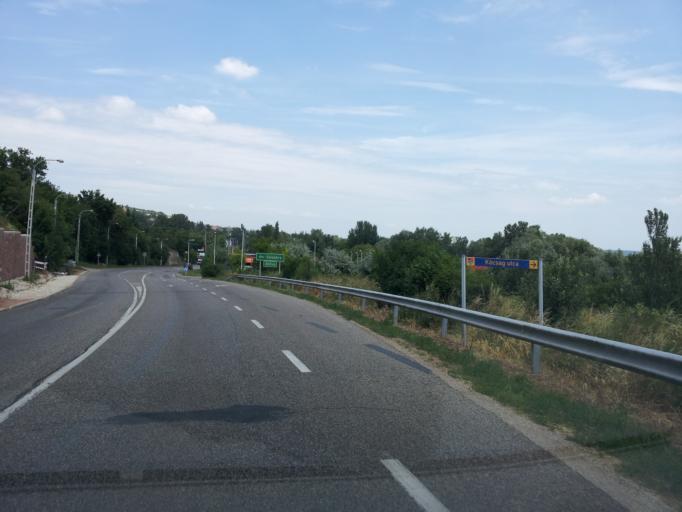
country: HU
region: Veszprem
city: Balatonalmadi
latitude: 47.0144
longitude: 18.0064
